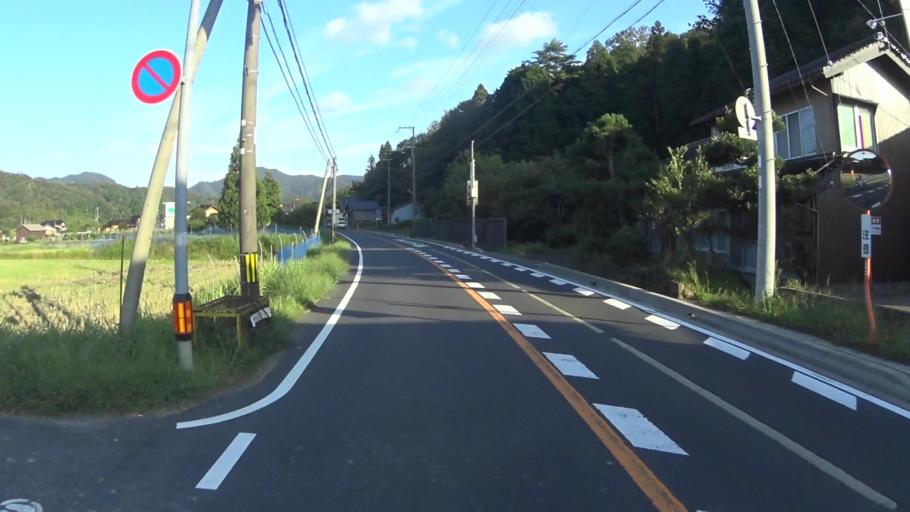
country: JP
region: Hyogo
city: Toyooka
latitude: 35.5815
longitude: 134.9637
